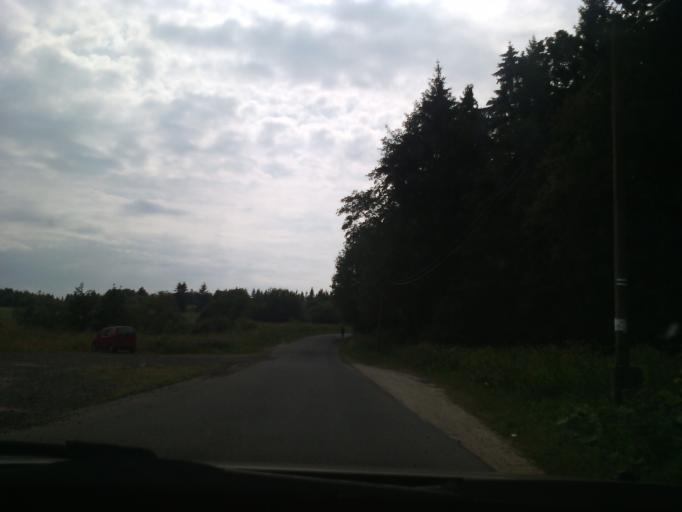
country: CZ
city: Mezimesti
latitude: 50.6871
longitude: 16.2767
